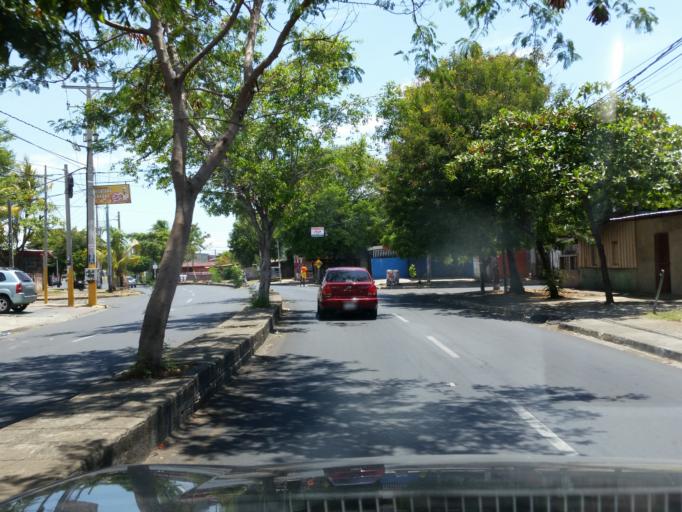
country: NI
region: Managua
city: Managua
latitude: 12.1466
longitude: -86.2389
